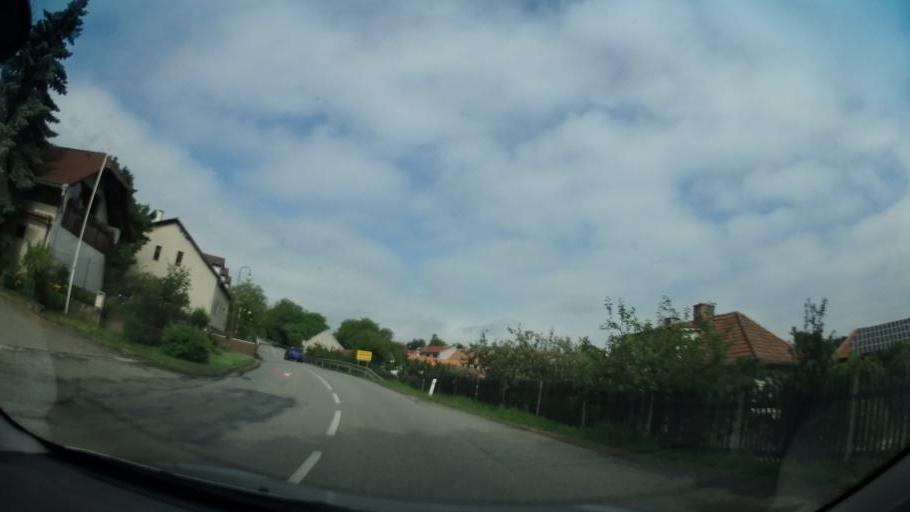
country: CZ
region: South Moravian
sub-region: Okres Brno-Venkov
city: Dolni Loucky
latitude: 49.3784
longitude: 16.3521
